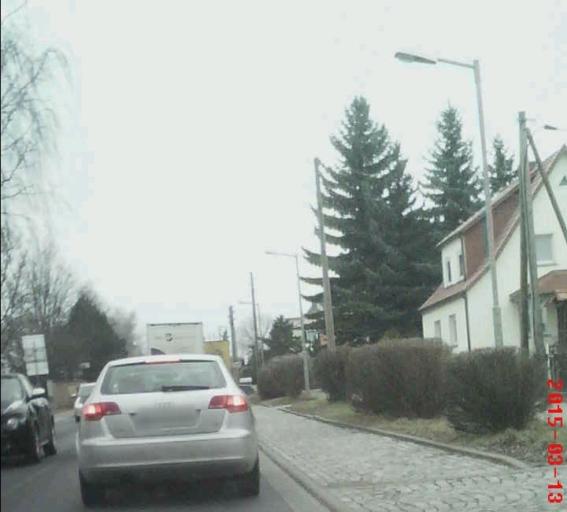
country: DE
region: Thuringia
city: Grossvargula
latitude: 51.0902
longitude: 10.7358
